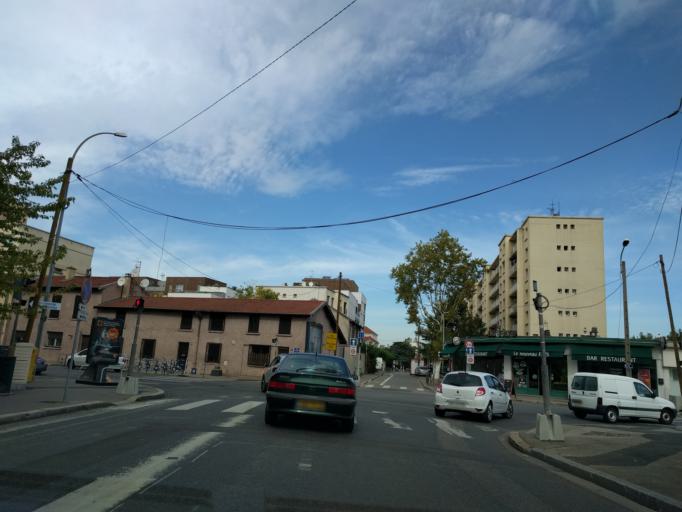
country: FR
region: Rhone-Alpes
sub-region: Departement du Rhone
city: Villeurbanne
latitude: 45.7604
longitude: 4.9057
